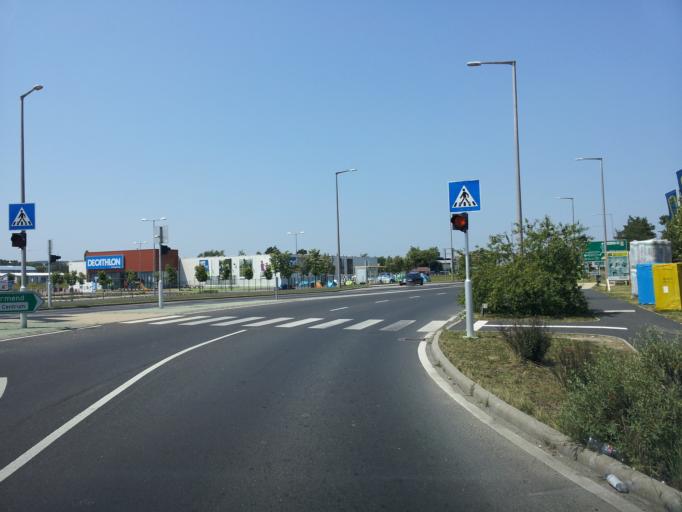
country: HU
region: Zala
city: Zalaegerszeg
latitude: 46.8437
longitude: 16.8685
